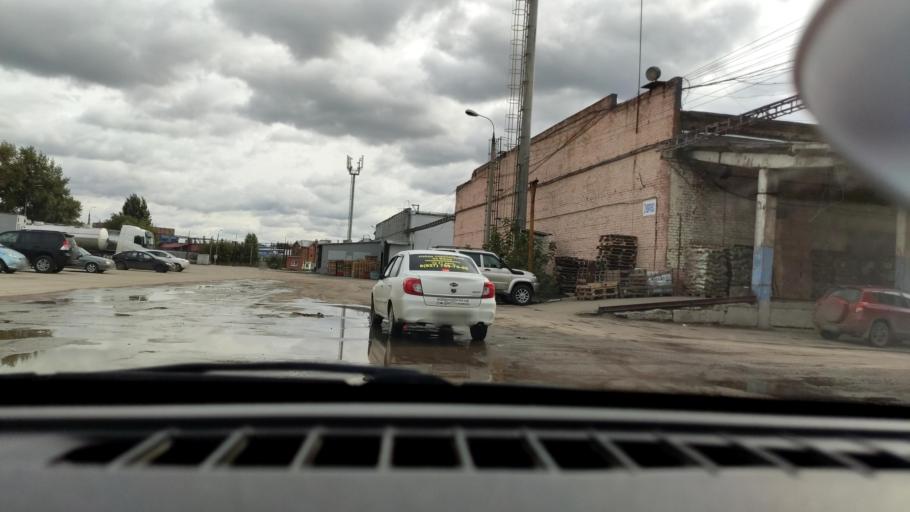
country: RU
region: Samara
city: Samara
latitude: 53.1921
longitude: 50.2361
